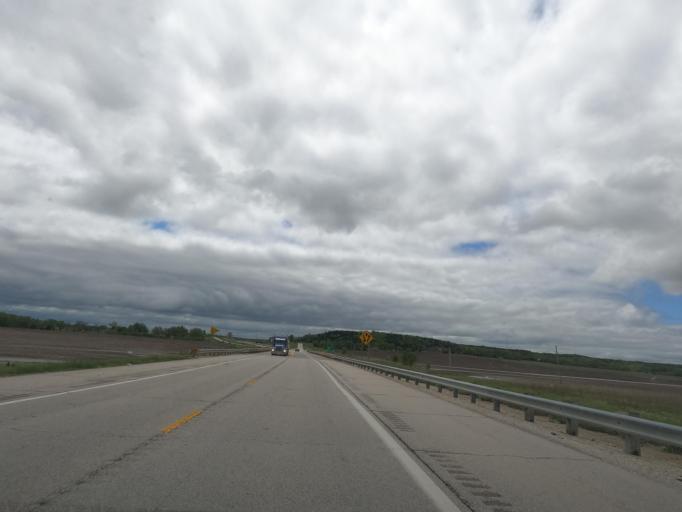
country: US
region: Kansas
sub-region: Wilson County
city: Neodesha
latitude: 37.4214
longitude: -95.7094
